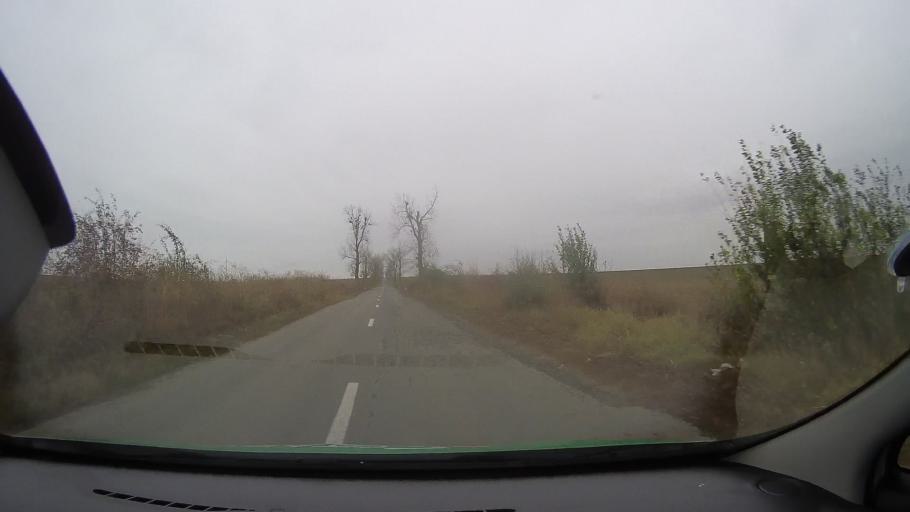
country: RO
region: Constanta
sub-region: Comuna Pantelimon
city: Pantelimon
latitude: 44.5564
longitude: 28.3246
